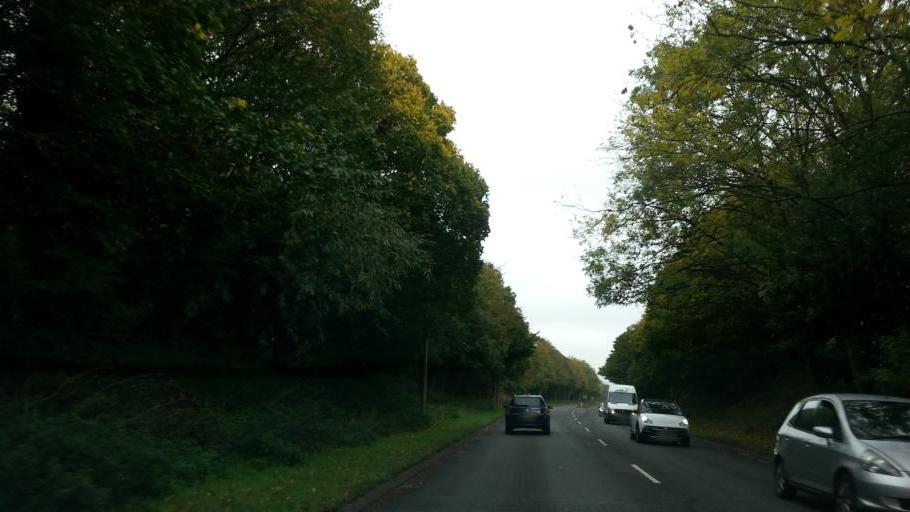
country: GB
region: England
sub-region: Worcestershire
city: Bromsgrove
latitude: 52.3266
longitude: -2.0566
